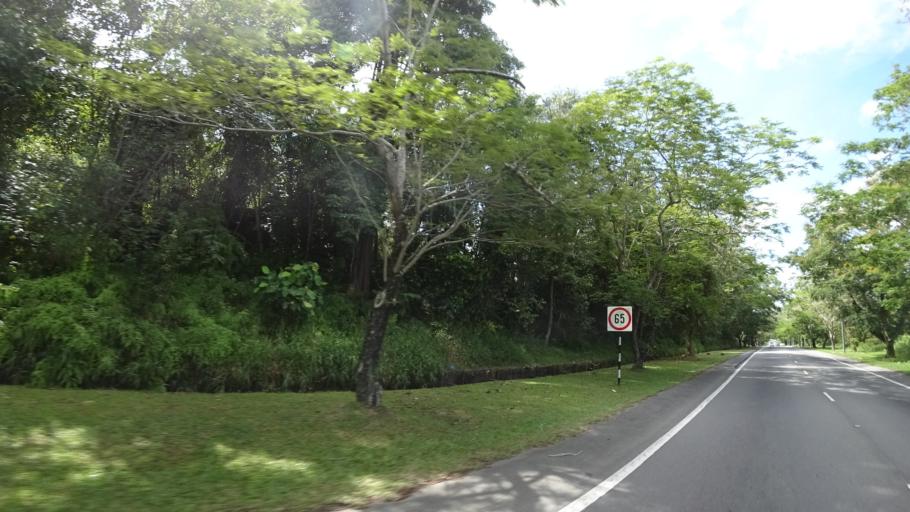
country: BN
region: Brunei and Muara
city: Bandar Seri Begawan
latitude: 4.8705
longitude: 114.9005
